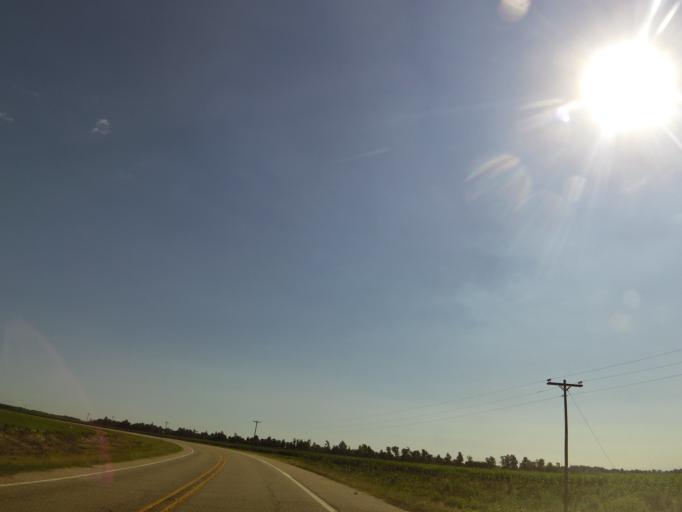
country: US
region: Arkansas
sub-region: Clay County
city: Corning
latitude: 36.4161
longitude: -90.4757
